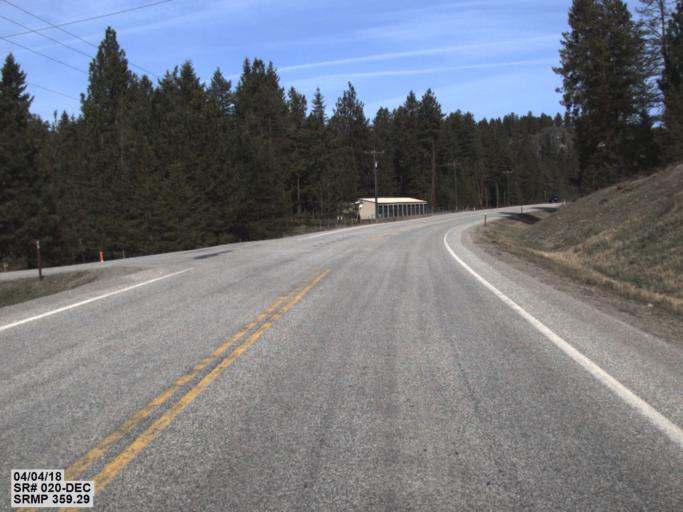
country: US
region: Washington
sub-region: Stevens County
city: Colville
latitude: 48.5249
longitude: -117.8173
